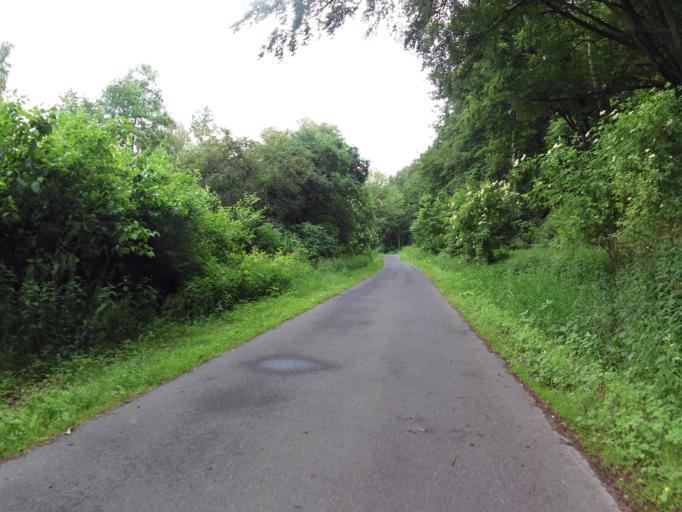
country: DE
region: Hesse
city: Breitenbach
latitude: 50.9729
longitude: 9.7665
